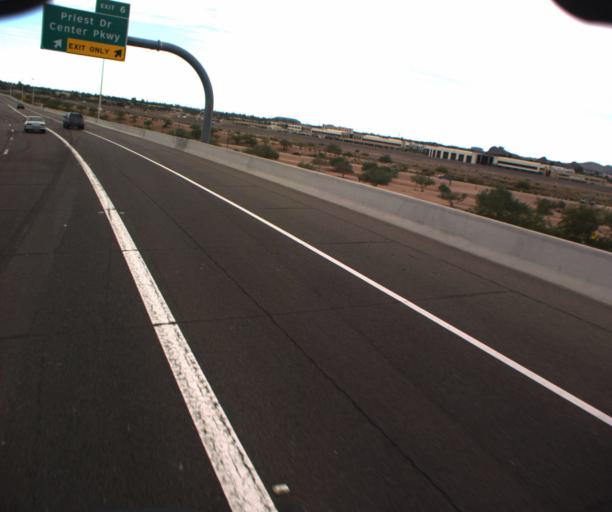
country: US
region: Arizona
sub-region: Maricopa County
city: Tempe Junction
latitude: 33.4403
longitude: -111.9677
